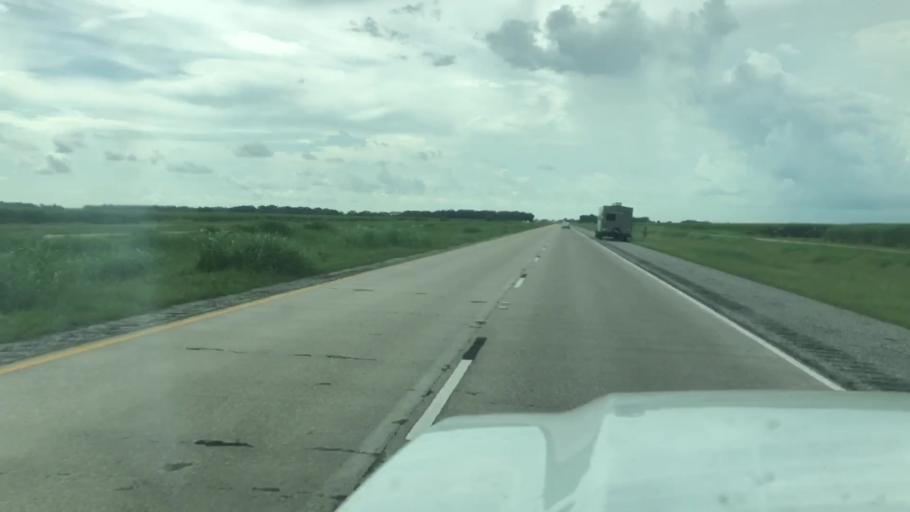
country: US
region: Louisiana
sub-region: Saint Mary Parish
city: Baldwin
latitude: 29.8494
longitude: -91.5943
